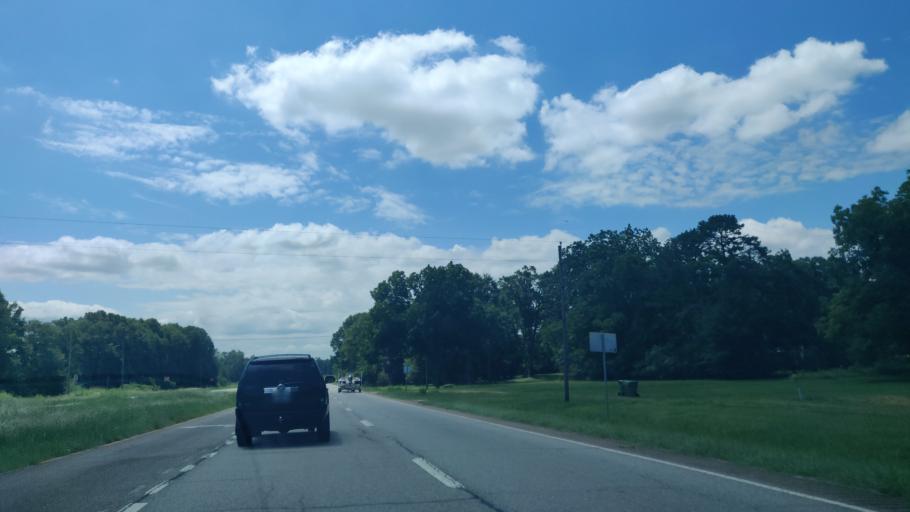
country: US
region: Georgia
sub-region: Stewart County
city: Richland
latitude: 32.0056
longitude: -84.6500
